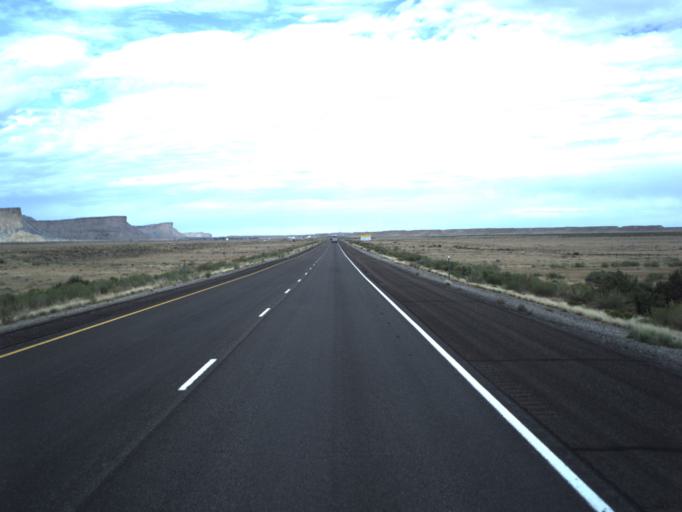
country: US
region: Utah
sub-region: Grand County
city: Moab
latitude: 38.9469
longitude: -109.7893
